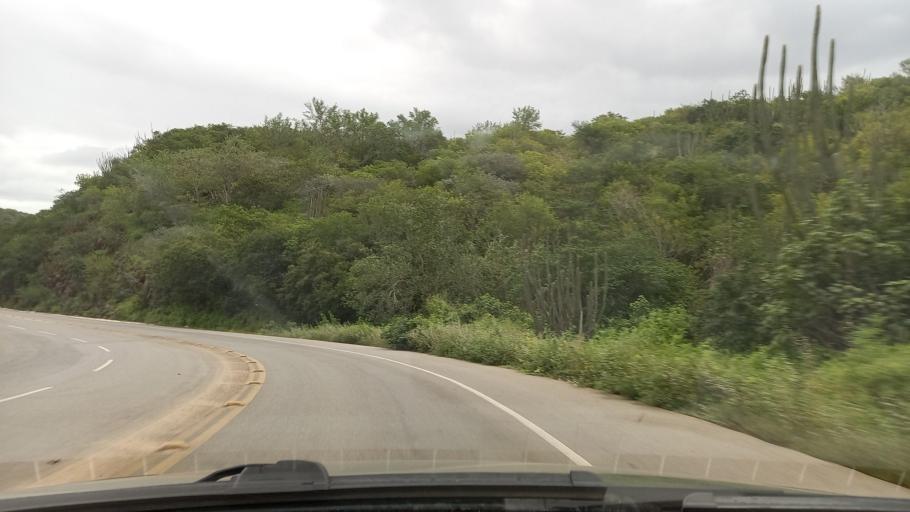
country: BR
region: Sergipe
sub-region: Caninde De Sao Francisco
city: Caninde de Sao Francisco
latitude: -9.6488
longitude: -37.7961
